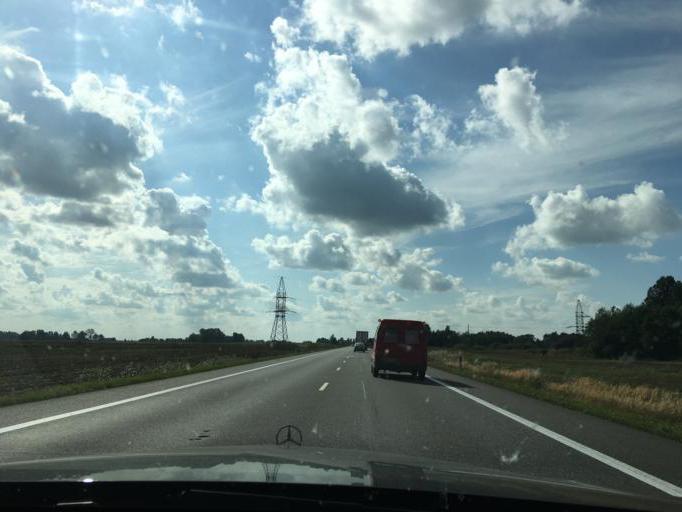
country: LT
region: Kauno apskritis
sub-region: Kauno rajonas
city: Mastaiciai
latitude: 54.7363
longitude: 23.7056
